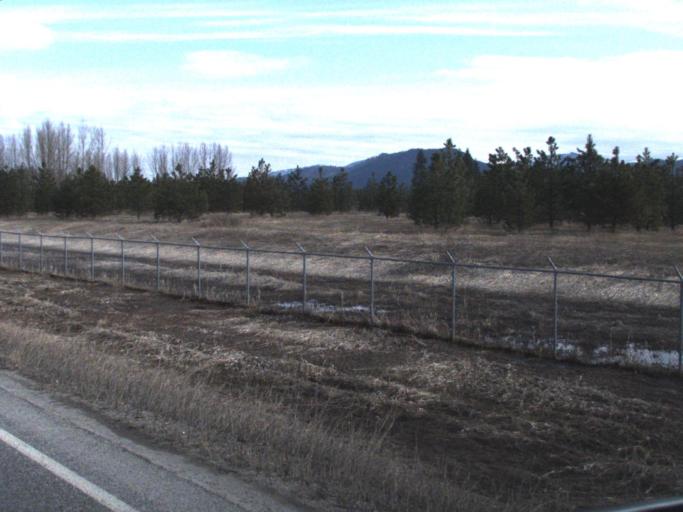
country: US
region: Washington
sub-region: Pend Oreille County
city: Newport
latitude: 48.2927
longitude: -117.2756
